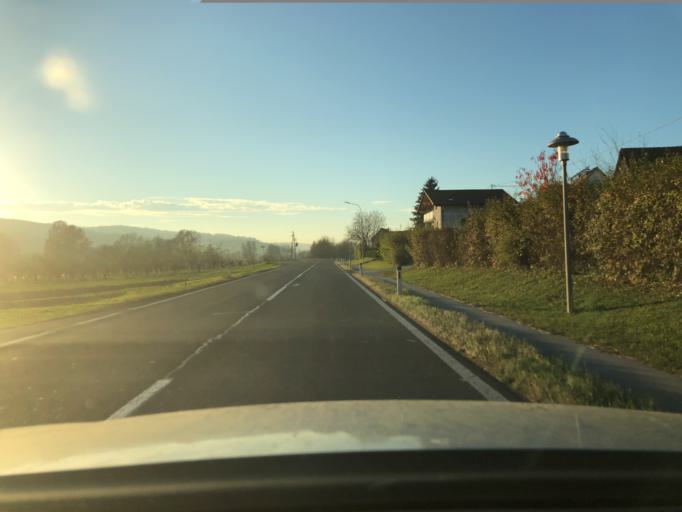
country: AT
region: Styria
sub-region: Politischer Bezirk Weiz
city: Sinabelkirchen
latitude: 47.0995
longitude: 15.8374
